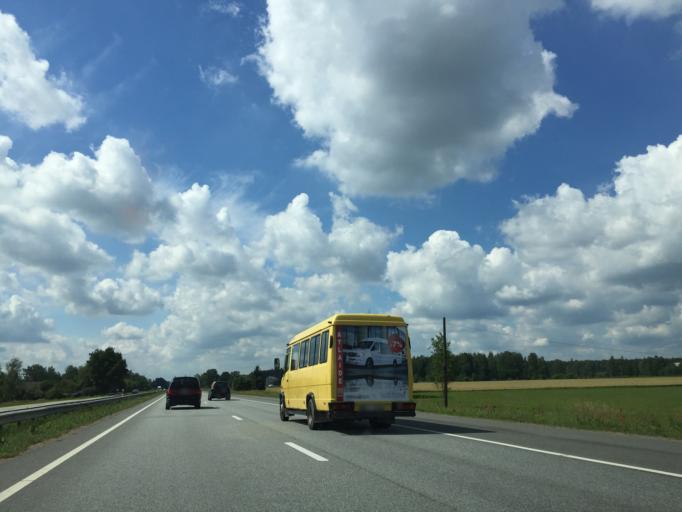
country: LV
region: Olaine
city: Olaine
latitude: 56.7728
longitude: 23.9286
